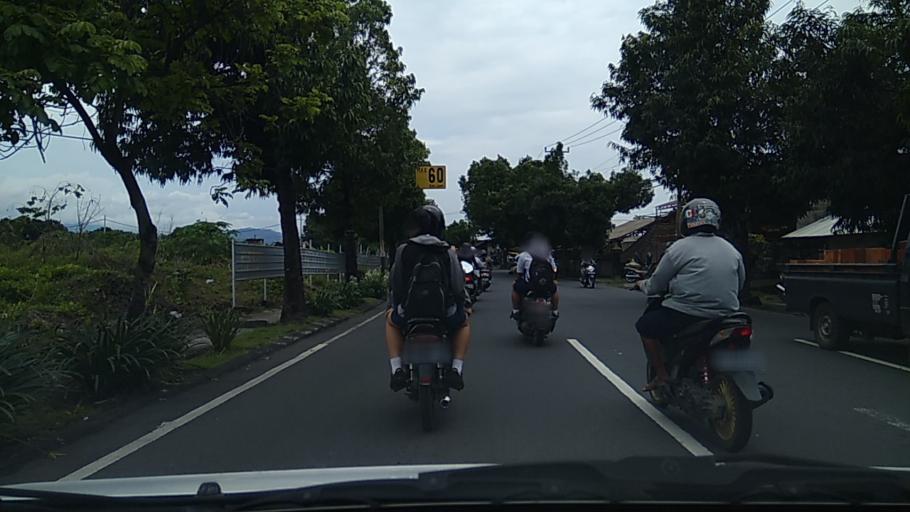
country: ID
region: Bali
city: Banjar Kelodan
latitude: -8.5402
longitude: 115.3379
